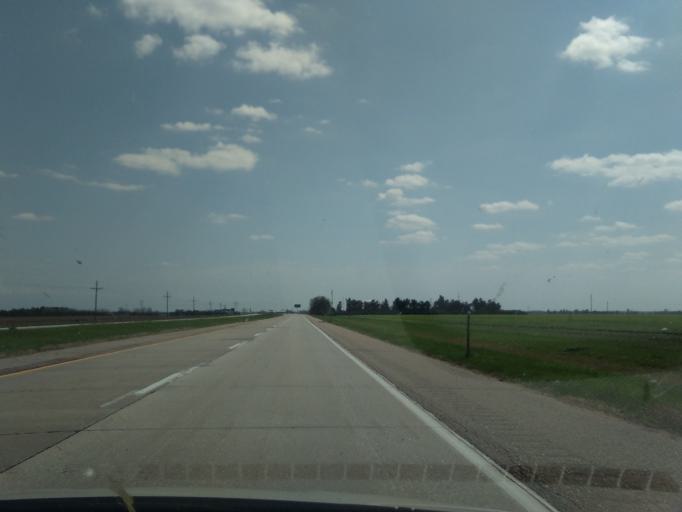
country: US
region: Nebraska
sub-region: Thayer County
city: Hebron
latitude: 40.1957
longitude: -97.5768
